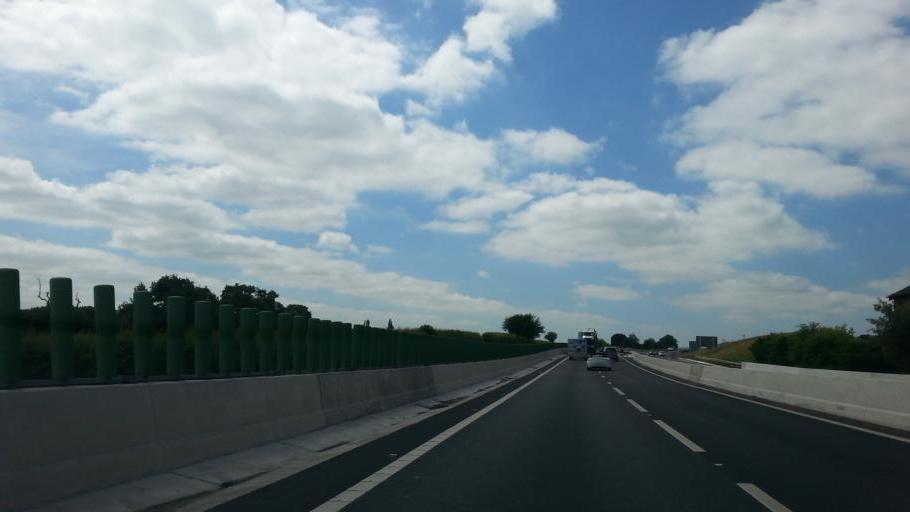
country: GB
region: England
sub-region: Cheshire East
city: Mere
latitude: 53.3600
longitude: -2.3949
